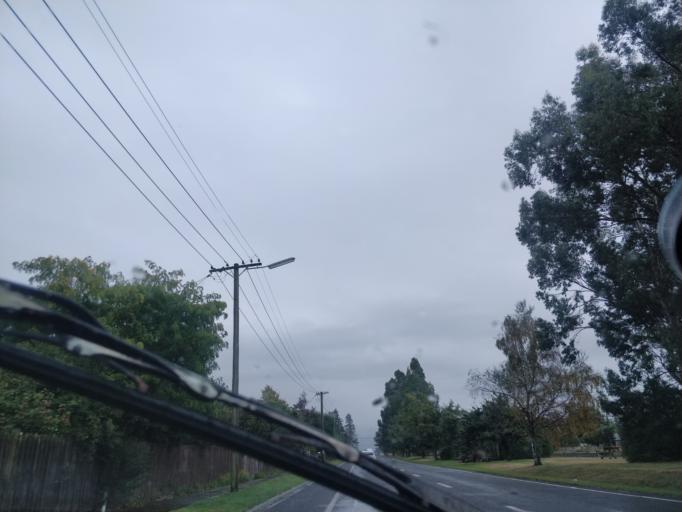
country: NZ
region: Canterbury
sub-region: Selwyn District
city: Darfield
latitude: -43.3884
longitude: 172.0185
